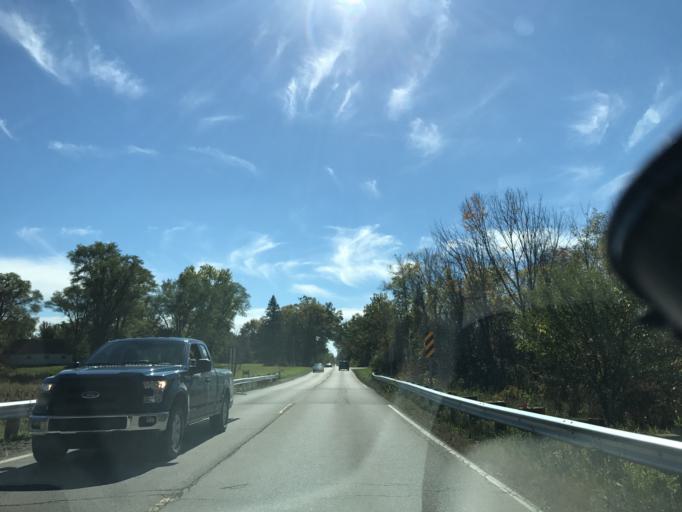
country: US
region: Michigan
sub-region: Oakland County
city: South Lyon
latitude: 42.4200
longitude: -83.6469
